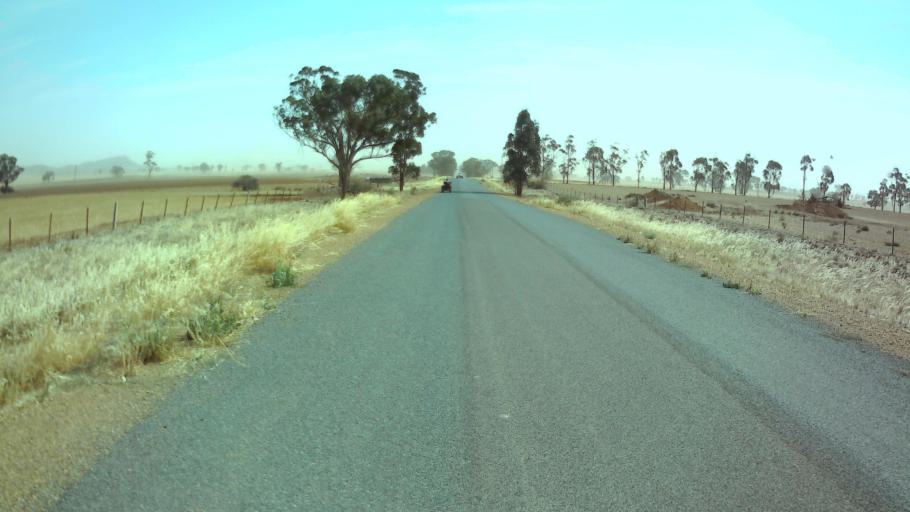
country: AU
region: New South Wales
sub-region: Weddin
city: Grenfell
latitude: -33.7672
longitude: 147.9876
